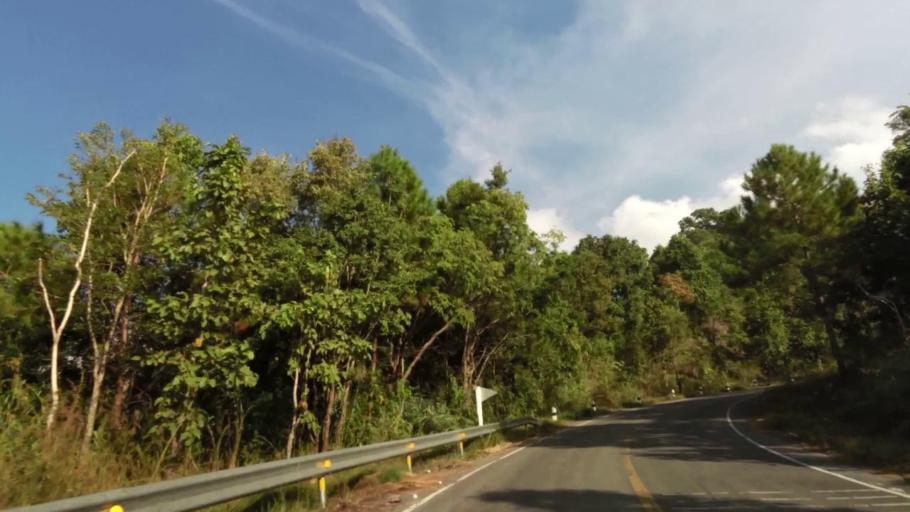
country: TH
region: Chiang Rai
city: Khun Tan
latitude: 19.8778
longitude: 100.3138
